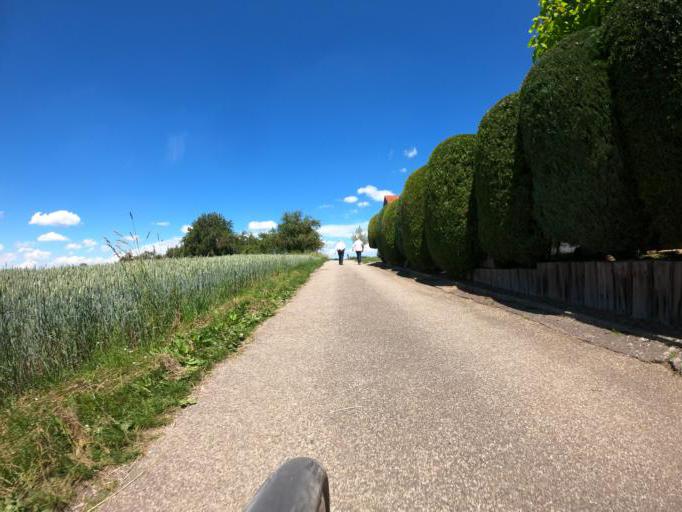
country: DE
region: Baden-Wuerttemberg
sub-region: Regierungsbezirk Stuttgart
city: Sersheim
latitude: 48.9663
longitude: 9.0134
